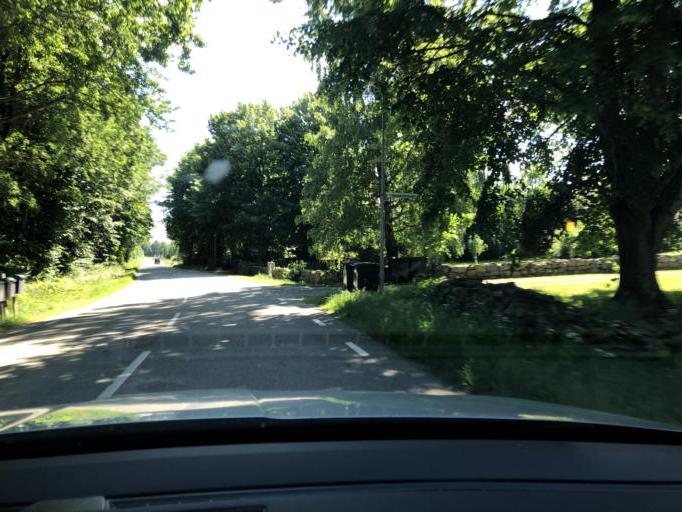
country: SE
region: Blekinge
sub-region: Solvesborgs Kommun
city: Soelvesborg
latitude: 56.1096
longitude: 14.6202
